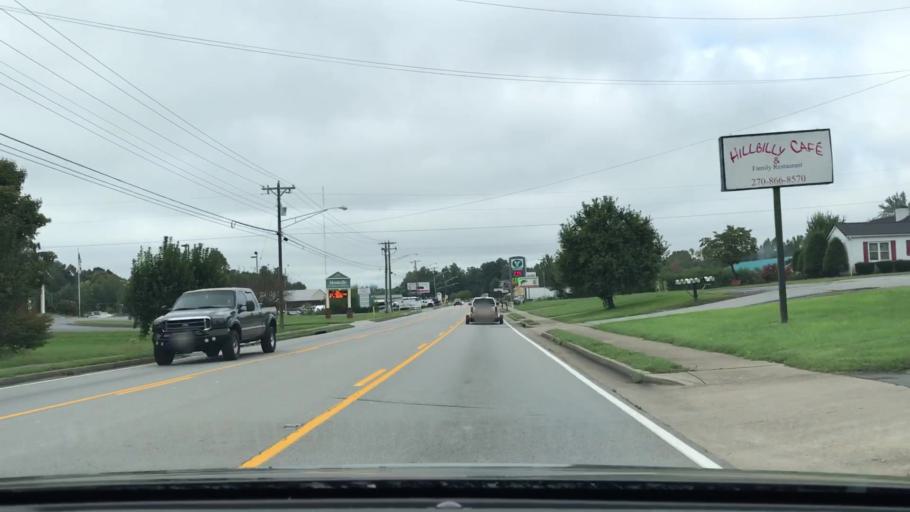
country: US
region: Kentucky
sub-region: Russell County
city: Russell Springs
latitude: 37.0310
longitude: -85.0767
